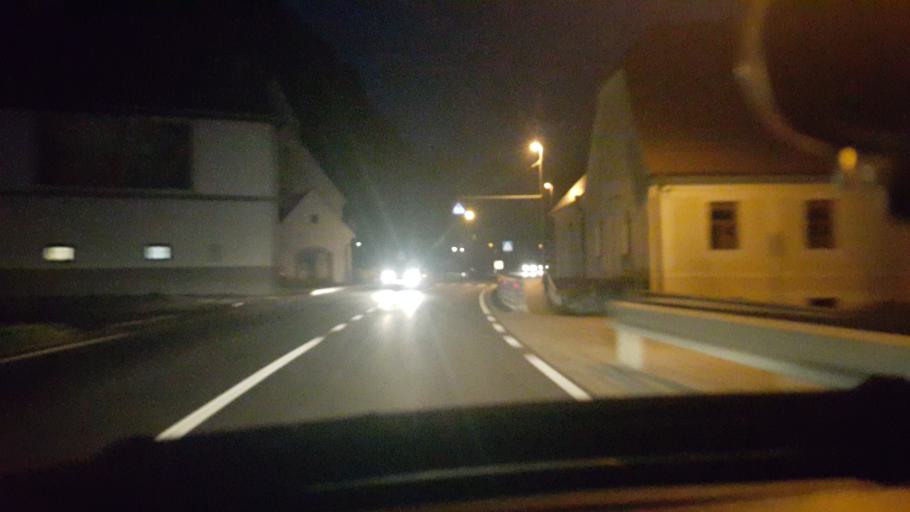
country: SI
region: Podvelka
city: Podvelka
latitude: 46.5964
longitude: 15.3166
